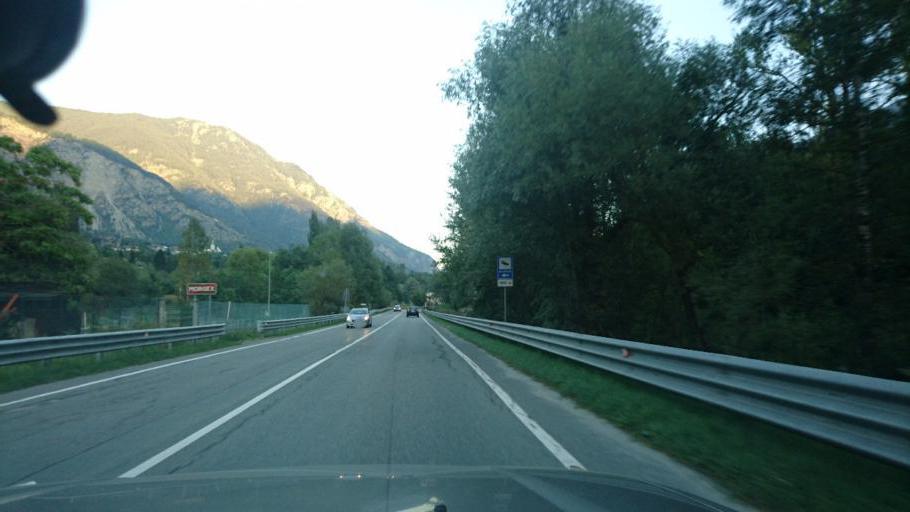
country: IT
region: Aosta Valley
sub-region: Valle d'Aosta
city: La Salle
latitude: 45.7481
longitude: 7.0564
